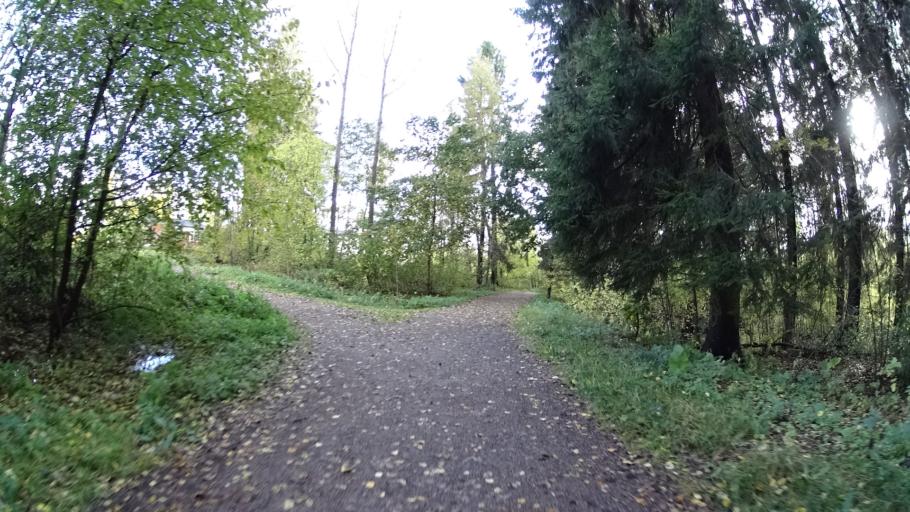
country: FI
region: Uusimaa
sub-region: Helsinki
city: Kilo
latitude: 60.2703
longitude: 24.8174
